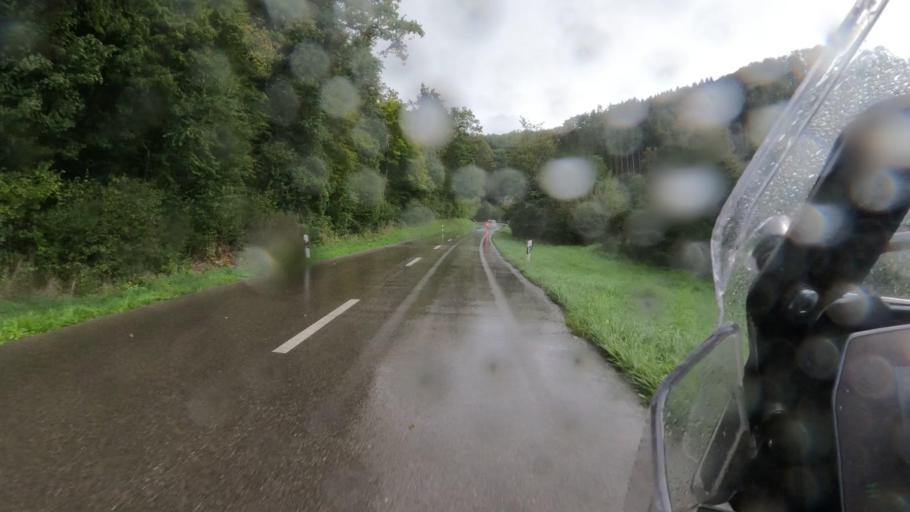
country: DE
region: Baden-Wuerttemberg
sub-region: Freiburg Region
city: Jestetten
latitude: 47.6469
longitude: 8.5206
